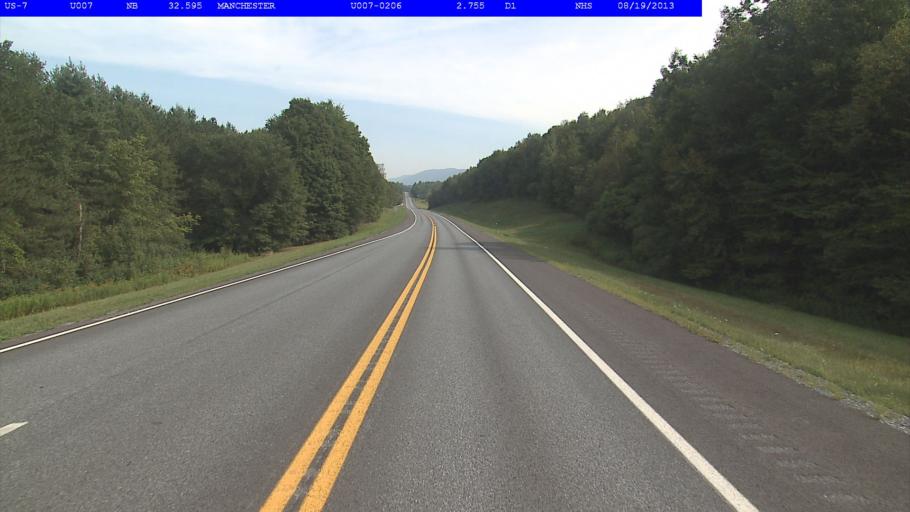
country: US
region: Vermont
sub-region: Bennington County
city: Manchester Center
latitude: 43.1494
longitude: -73.0477
